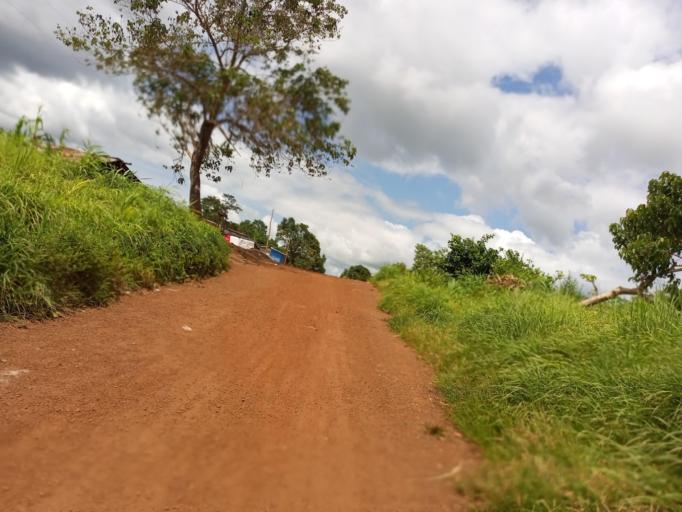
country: SL
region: Northern Province
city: Kamakwie
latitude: 9.5011
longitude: -12.2375
